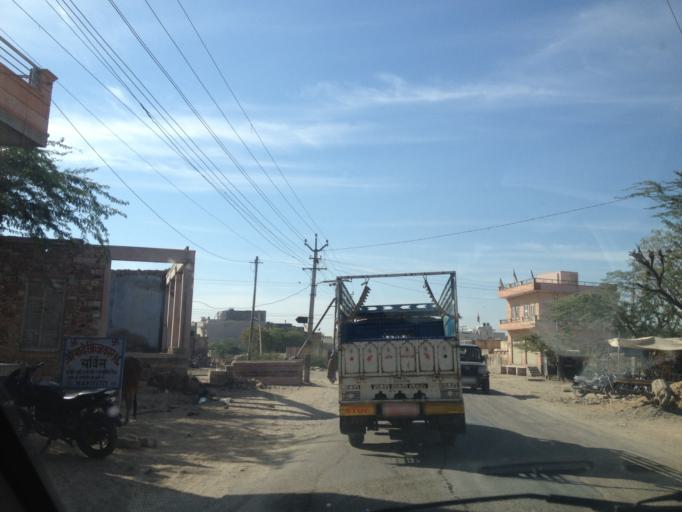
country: IN
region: Rajasthan
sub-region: Nagaur
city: Merta
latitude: 26.6465
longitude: 74.0277
